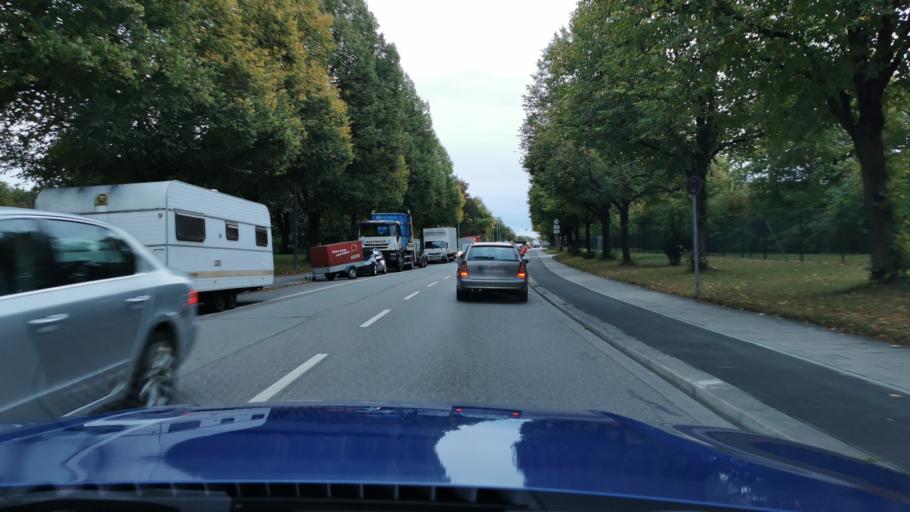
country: DE
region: Bavaria
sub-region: Upper Bavaria
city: Oberschleissheim
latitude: 48.2111
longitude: 11.5785
